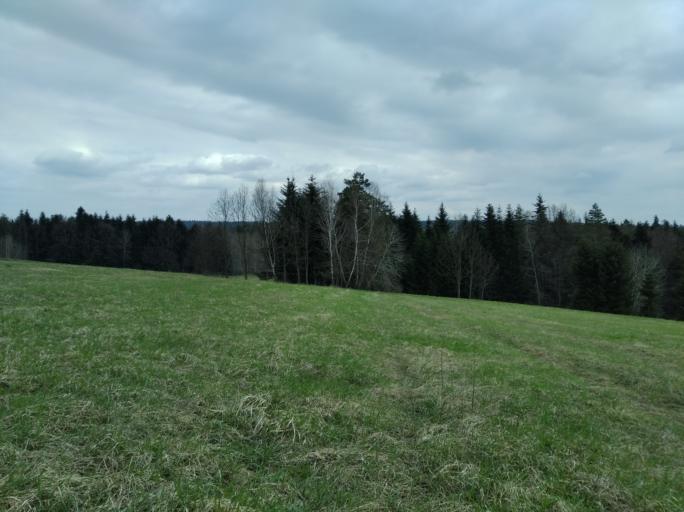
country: PL
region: Subcarpathian Voivodeship
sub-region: Powiat strzyzowski
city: Wysoka Strzyzowska
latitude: 49.8035
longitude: 21.7690
